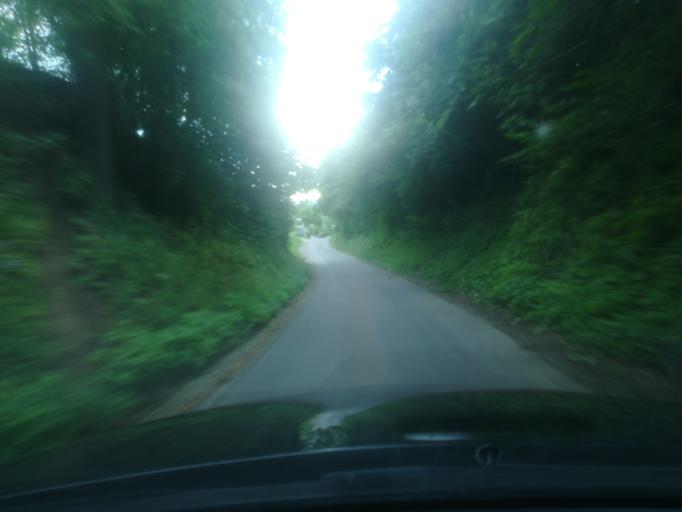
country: AT
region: Upper Austria
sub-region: Politischer Bezirk Urfahr-Umgebung
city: Ottensheim
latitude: 48.3219
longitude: 14.1809
